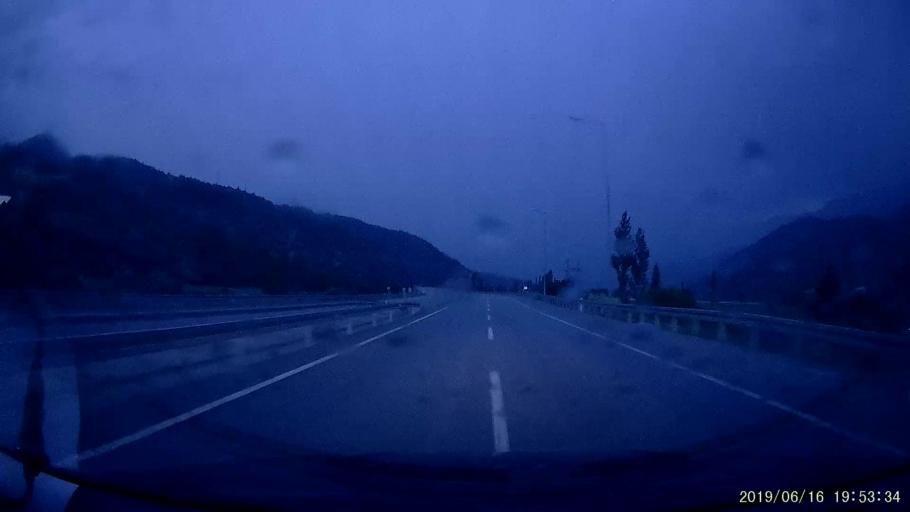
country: TR
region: Sivas
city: Koyulhisar
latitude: 40.2885
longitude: 37.7824
